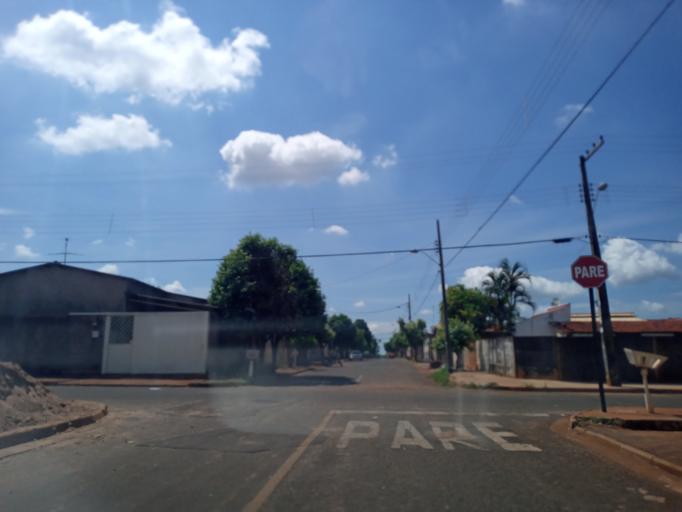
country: BR
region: Minas Gerais
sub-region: Ituiutaba
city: Ituiutaba
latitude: -18.9975
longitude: -49.4754
